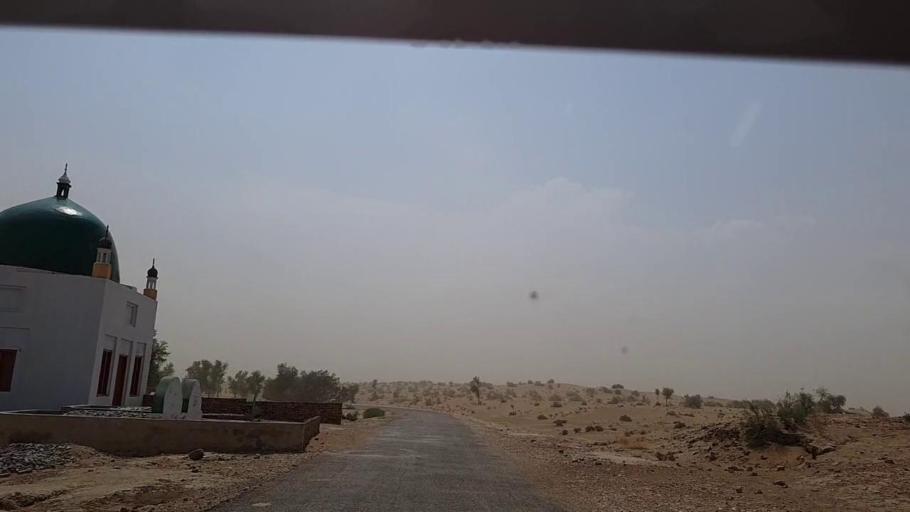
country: PK
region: Sindh
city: Phulji
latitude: 27.0005
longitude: 67.5039
